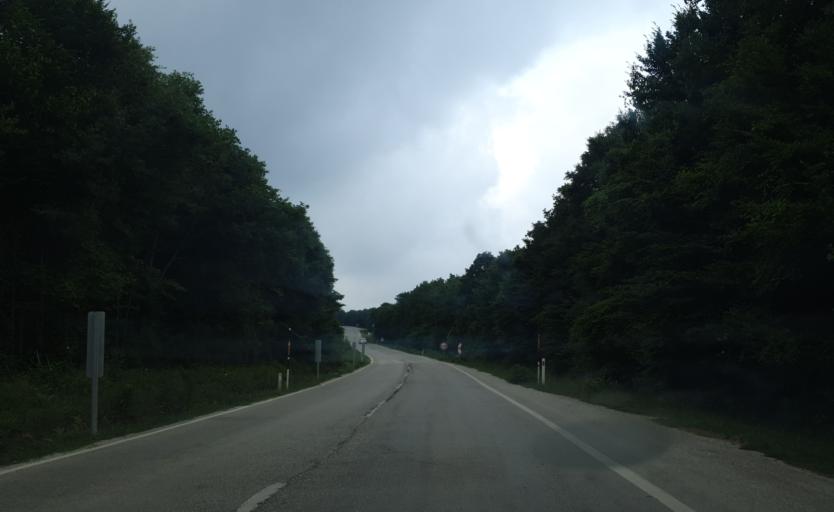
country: TR
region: Kirklareli
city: Salmydessus
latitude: 41.5686
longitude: 28.0765
